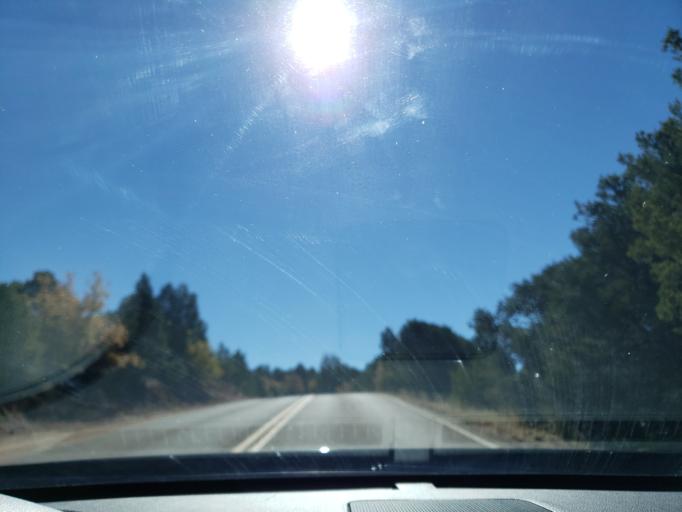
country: US
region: Colorado
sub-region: Fremont County
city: Canon City
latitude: 38.4751
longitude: -105.3074
